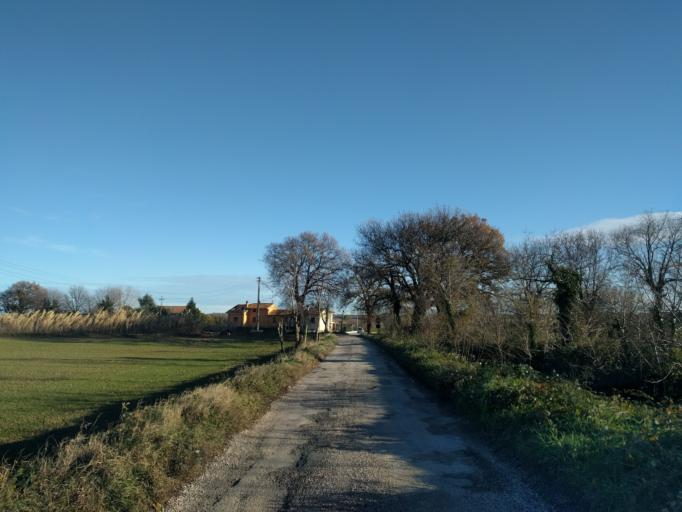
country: IT
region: The Marches
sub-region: Provincia di Pesaro e Urbino
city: Bellocchi
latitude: 43.7966
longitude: 12.9831
